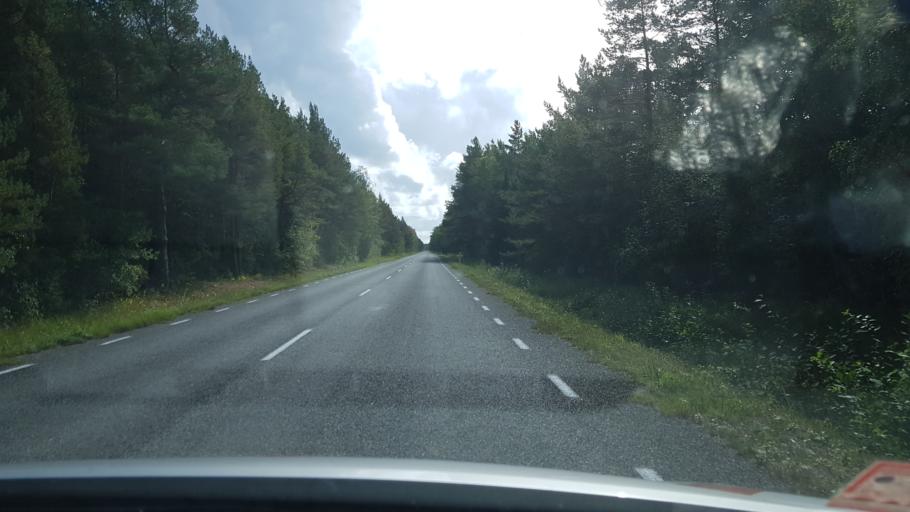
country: EE
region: Saare
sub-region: Kuressaare linn
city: Kuressaare
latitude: 58.3964
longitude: 22.0070
